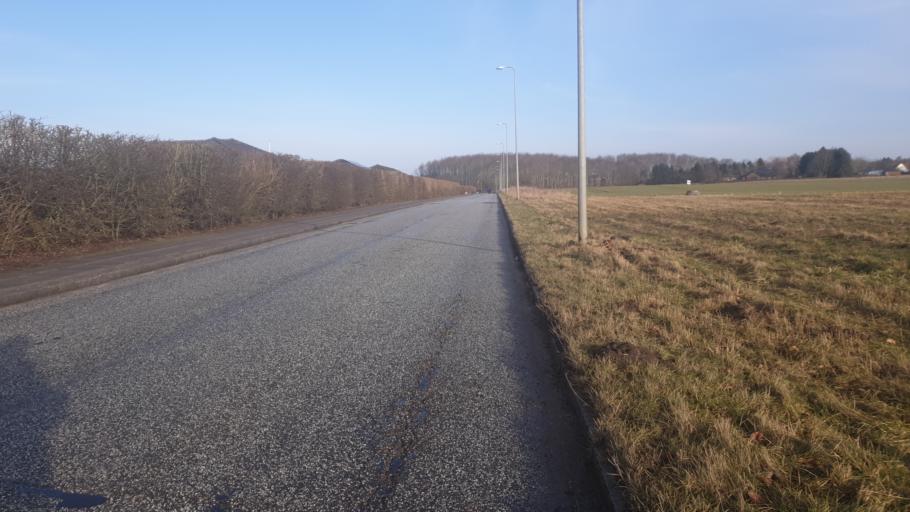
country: DK
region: Central Jutland
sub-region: Hedensted Kommune
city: Hedensted
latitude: 55.7697
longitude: 9.7202
